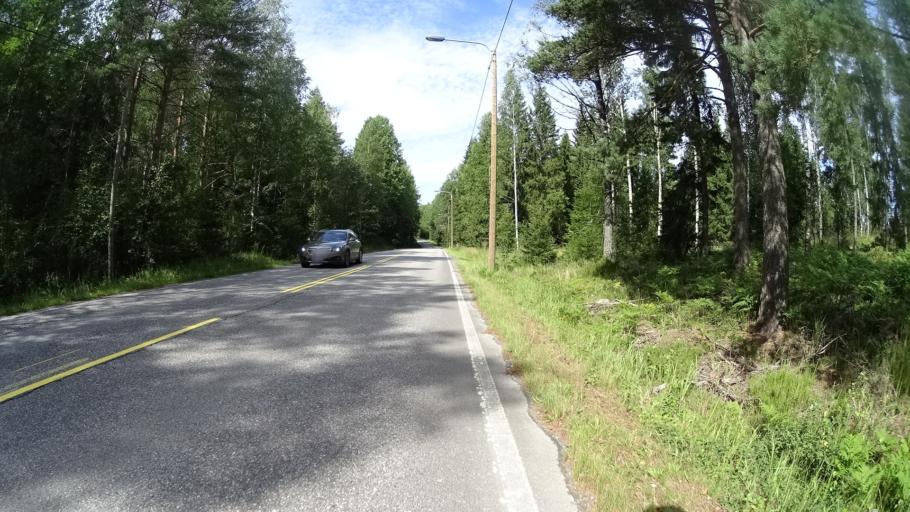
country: FI
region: Uusimaa
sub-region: Helsinki
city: Kirkkonummi
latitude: 60.1182
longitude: 24.5455
